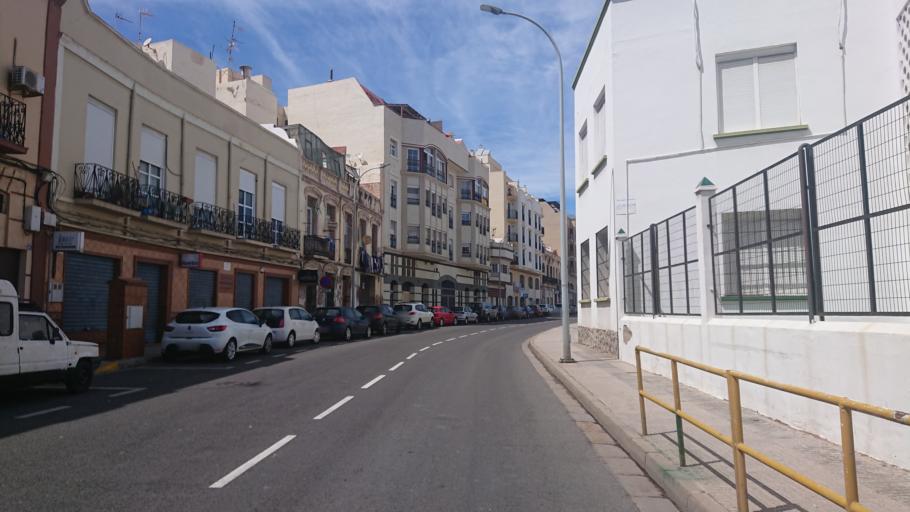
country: ES
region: Melilla
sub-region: Melilla
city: Melilla
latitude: 35.2847
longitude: -2.9415
